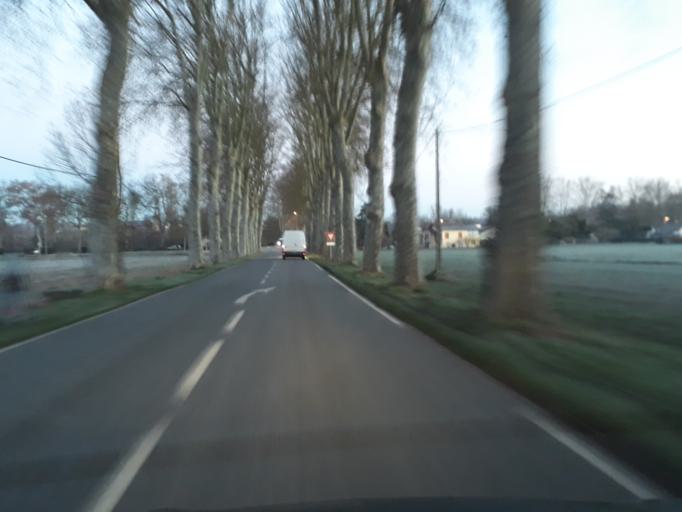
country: FR
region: Midi-Pyrenees
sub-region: Departement du Gers
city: Samatan
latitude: 43.4851
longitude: 0.9355
